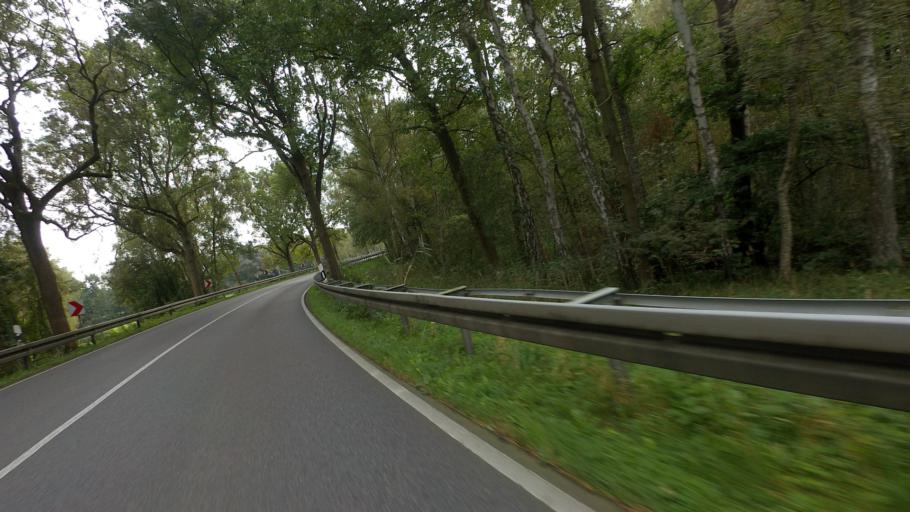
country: DE
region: Brandenburg
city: Luckau
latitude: 51.7940
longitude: 13.6891
